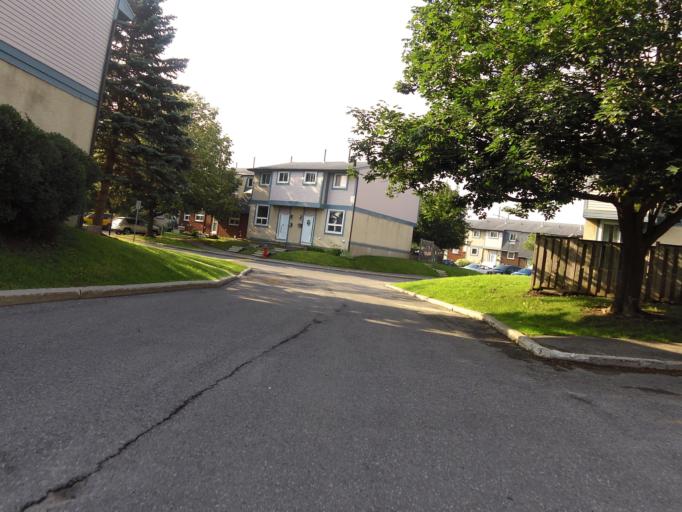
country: CA
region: Ontario
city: Ottawa
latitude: 45.3489
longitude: -75.6762
